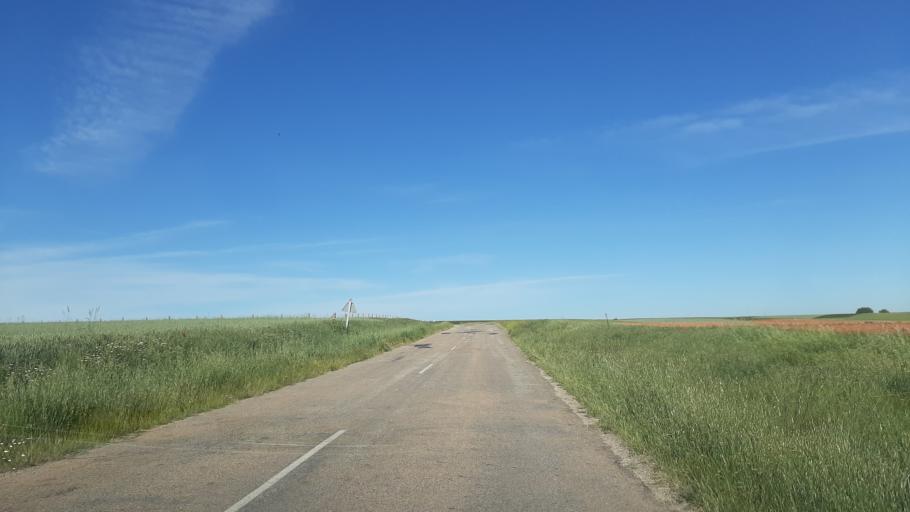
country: ES
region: Castille and Leon
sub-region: Provincia de Salamanca
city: Pedrosillo de Alba
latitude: 40.8230
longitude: -5.4014
